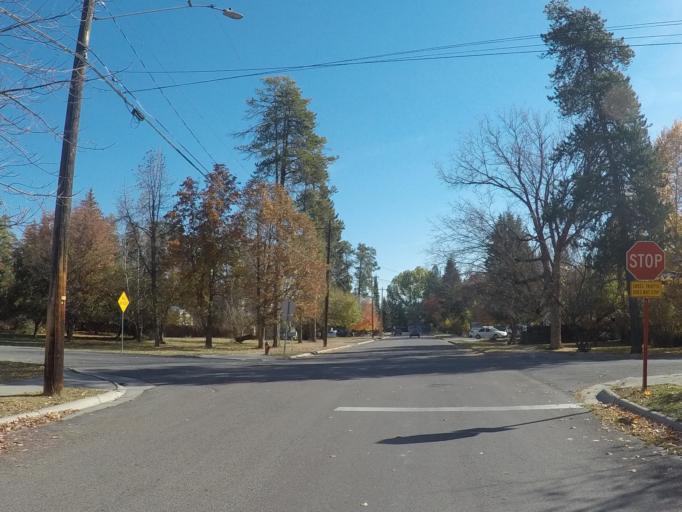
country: US
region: Montana
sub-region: Flathead County
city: Whitefish
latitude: 48.4180
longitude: -114.3441
